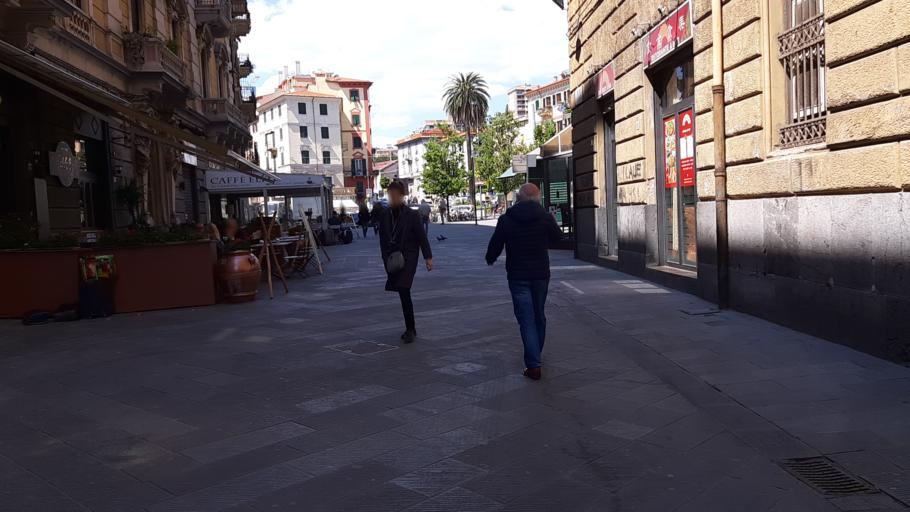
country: IT
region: Liguria
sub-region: Provincia di La Spezia
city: La Spezia
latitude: 44.1094
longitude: 9.8163
